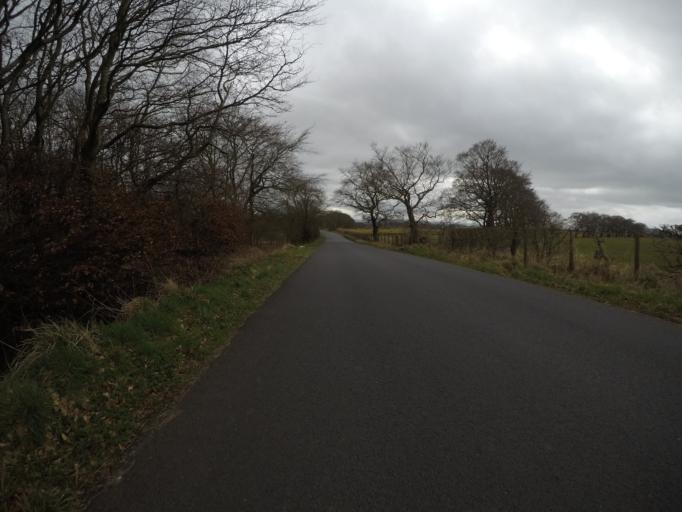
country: GB
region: Scotland
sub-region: East Ayrshire
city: Stewarton
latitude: 55.6796
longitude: -4.4410
